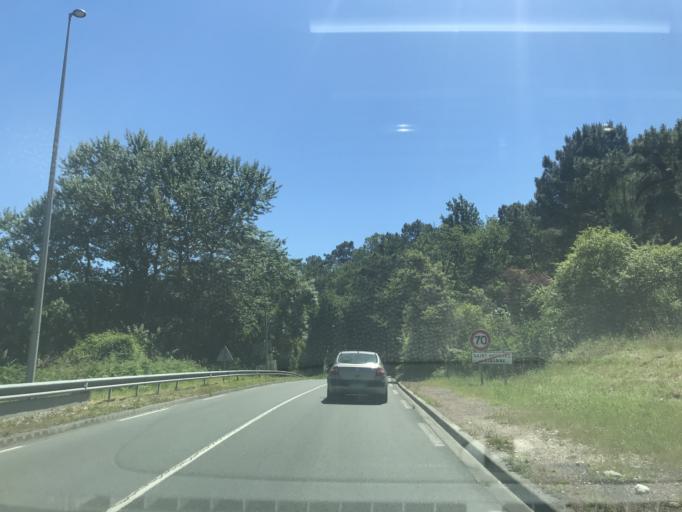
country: FR
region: Poitou-Charentes
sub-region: Departement de la Charente-Maritime
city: Saint-Georges-de-Didonne
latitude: 45.5956
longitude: -0.9741
